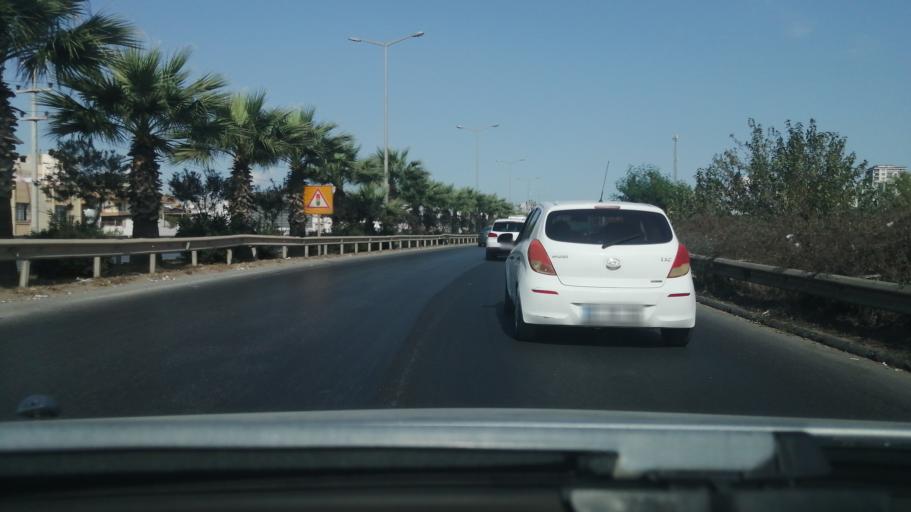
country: TR
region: Adana
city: Seyhan
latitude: 37.0294
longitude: 35.2556
